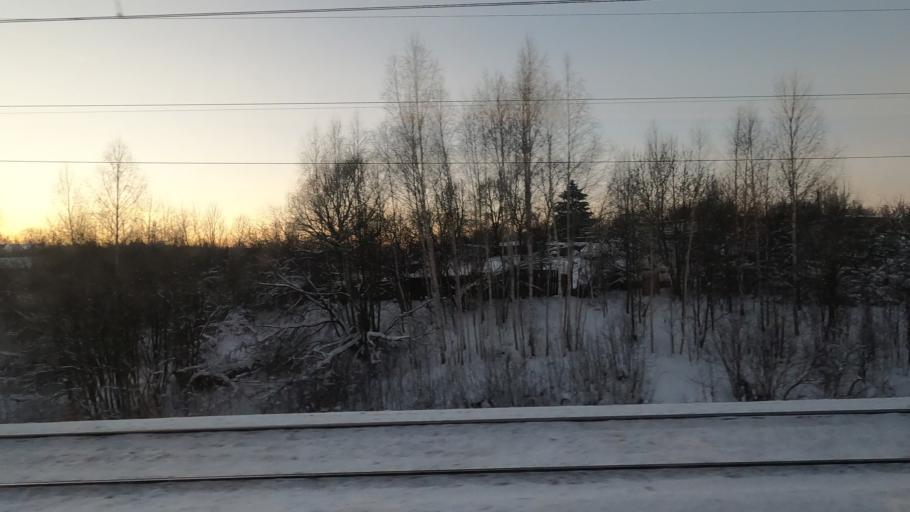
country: RU
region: Moskovskaya
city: Iksha
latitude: 56.1599
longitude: 37.5002
